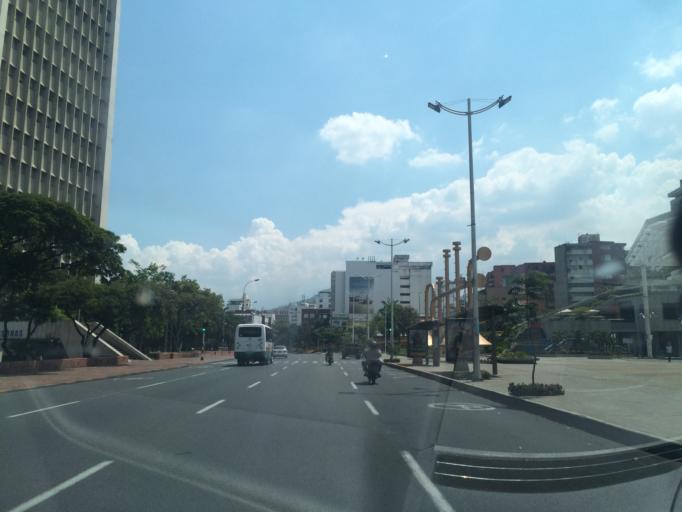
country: CO
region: Valle del Cauca
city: Cali
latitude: 3.4551
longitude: -76.5342
